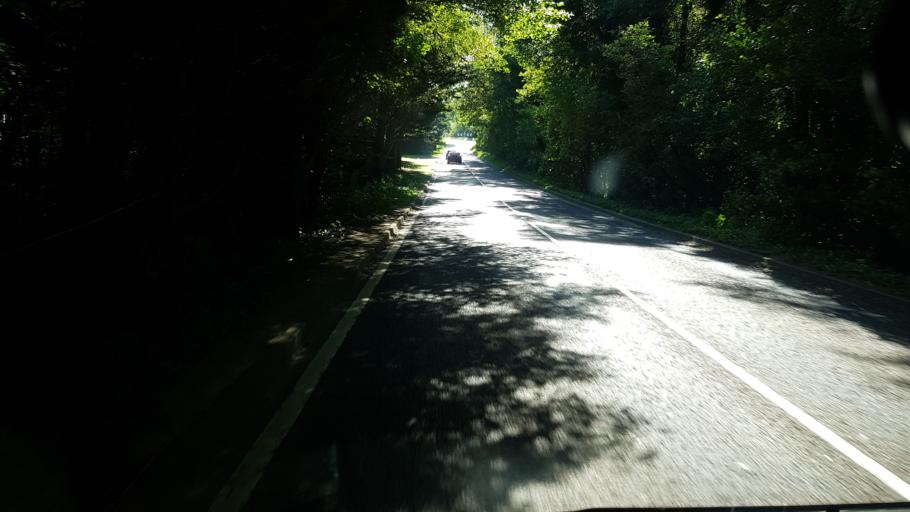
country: GB
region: England
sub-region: Kent
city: Kings Hill
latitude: 51.2533
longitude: 0.3719
